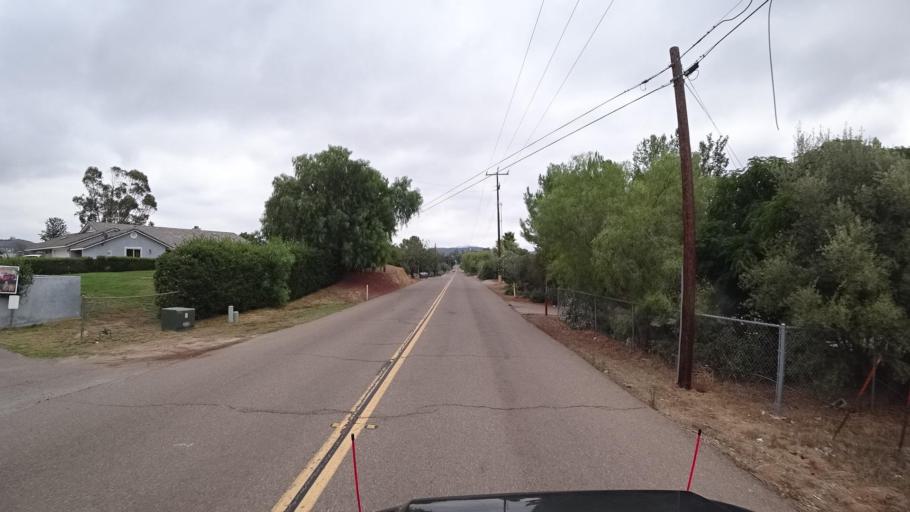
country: US
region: California
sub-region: San Diego County
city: Ramona
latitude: 33.0347
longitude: -116.8606
